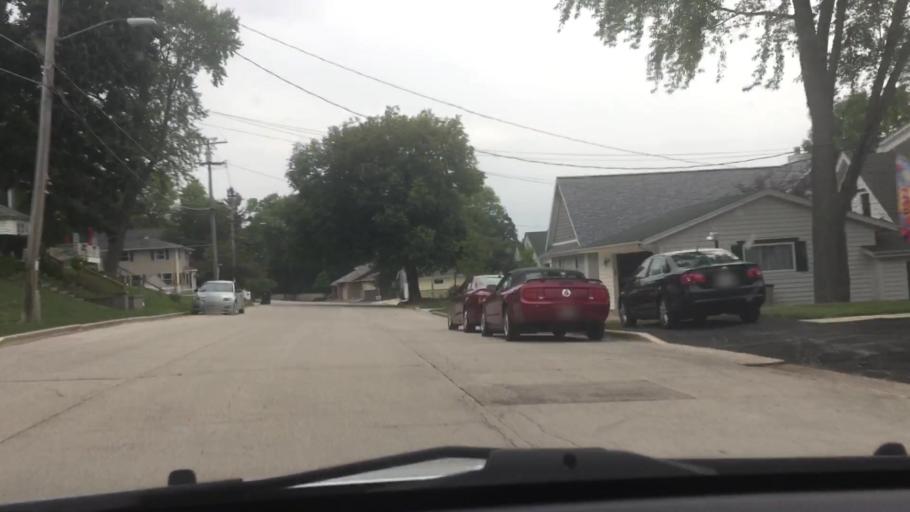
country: US
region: Wisconsin
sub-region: Waukesha County
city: Pewaukee
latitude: 43.0788
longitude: -88.2673
